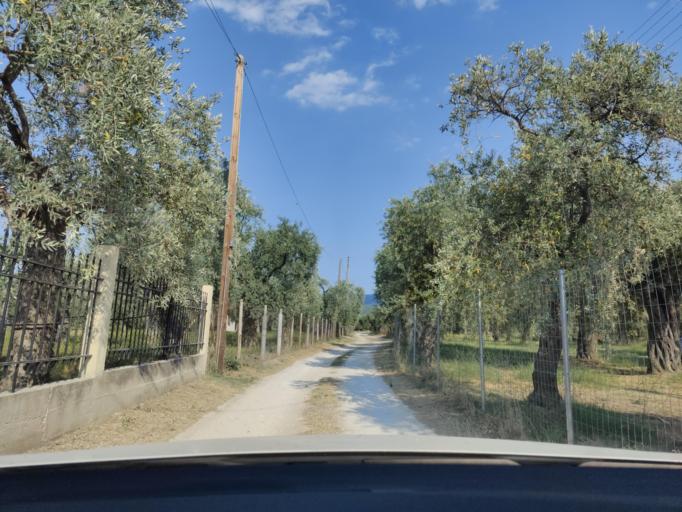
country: GR
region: East Macedonia and Thrace
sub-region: Nomos Kavalas
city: Prinos
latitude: 40.7698
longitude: 24.5953
